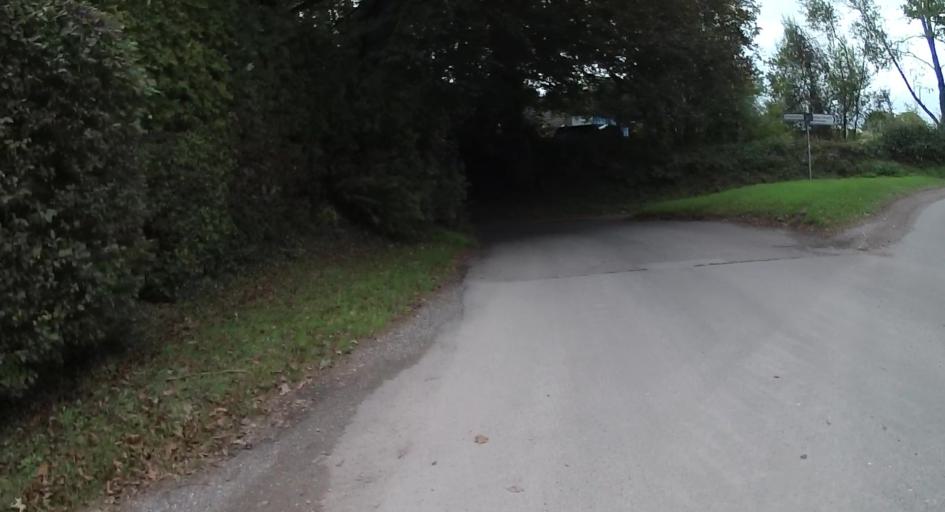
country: GB
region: England
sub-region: Hampshire
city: Alton
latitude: 51.1273
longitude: -0.9421
